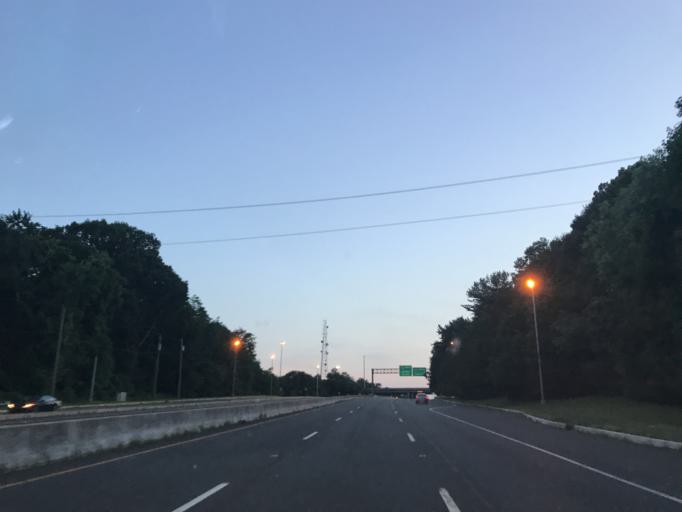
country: US
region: New Jersey
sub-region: Burlington County
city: Bordentown
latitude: 40.1372
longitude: -74.7117
